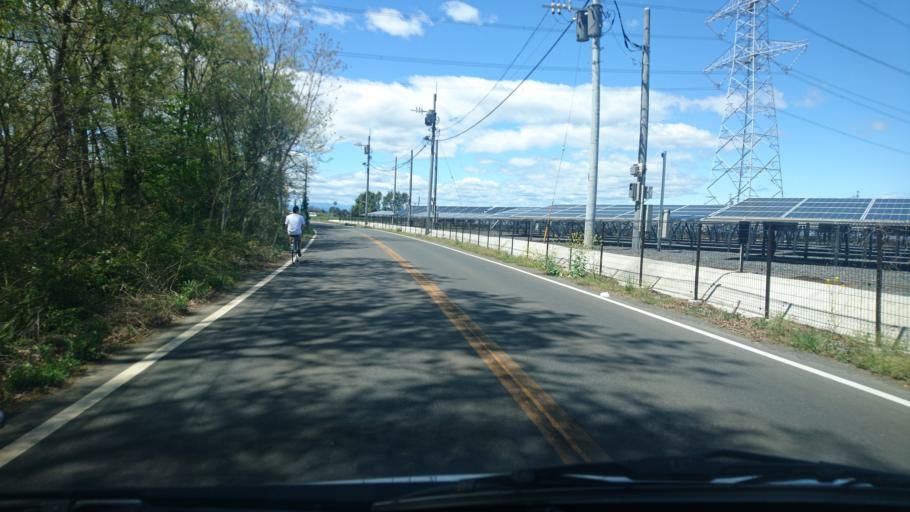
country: JP
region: Ibaraki
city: Yuki
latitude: 36.2748
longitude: 139.9196
